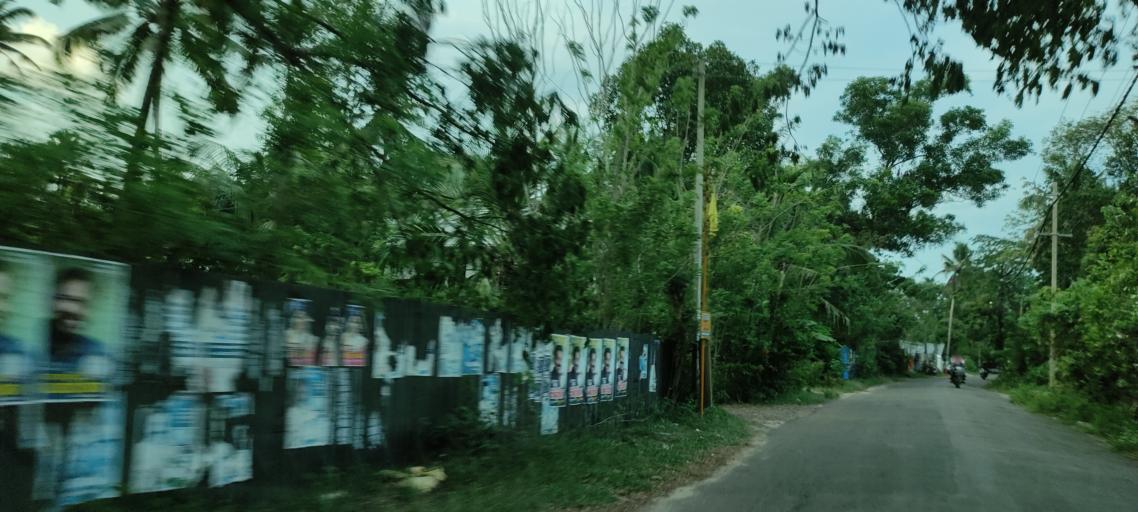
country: IN
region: Kerala
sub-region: Alappuzha
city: Shertallai
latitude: 9.6946
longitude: 76.3557
